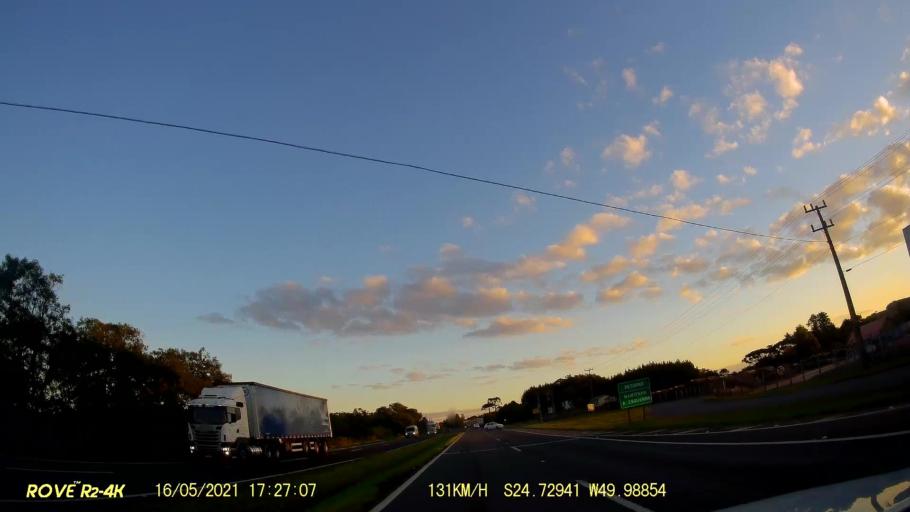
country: BR
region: Parana
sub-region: Castro
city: Castro
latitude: -24.7297
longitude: -49.9887
